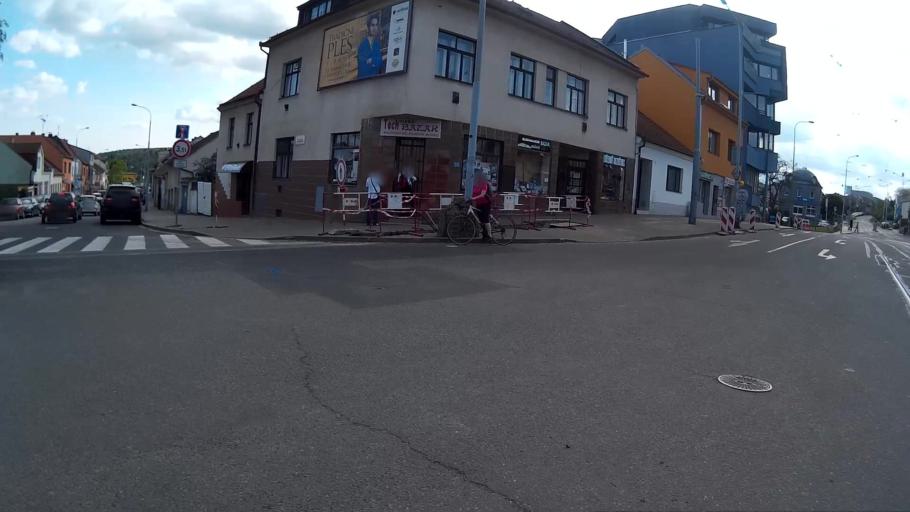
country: CZ
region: South Moravian
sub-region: Mesto Brno
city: Brno
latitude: 49.2146
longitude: 16.5697
